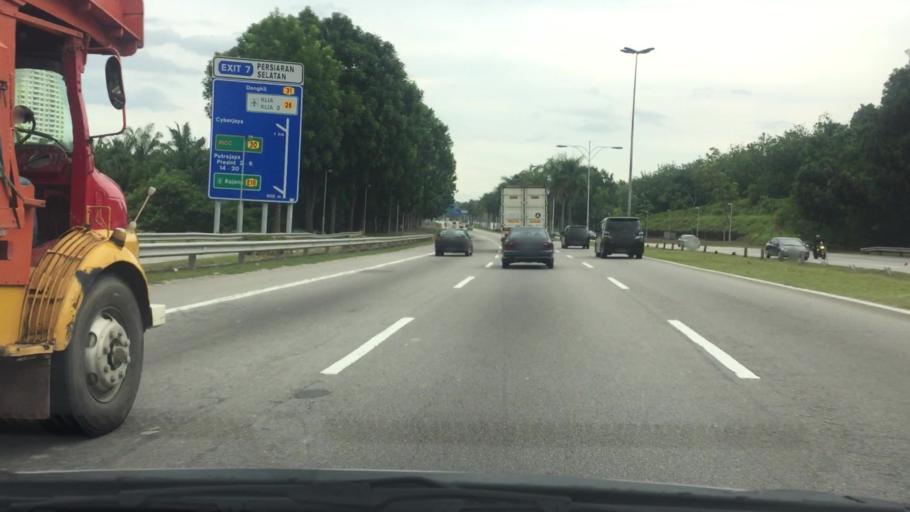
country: MY
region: Putrajaya
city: Putrajaya
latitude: 2.9045
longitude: 101.6584
